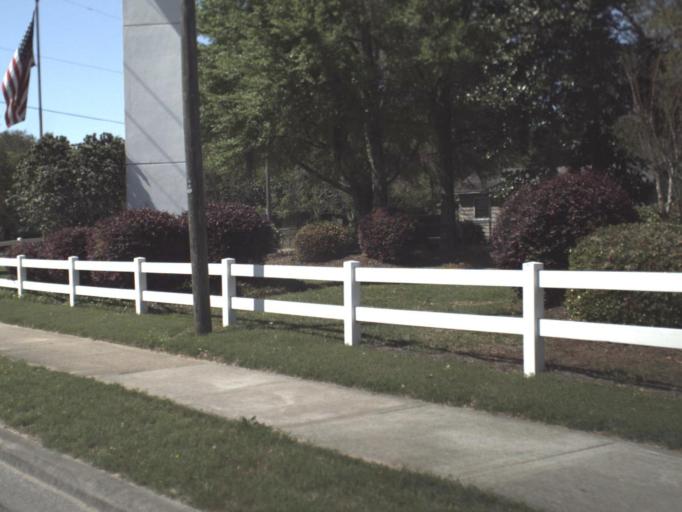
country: US
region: Florida
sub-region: Okaloosa County
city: Ocean City
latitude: 30.4479
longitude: -86.6108
